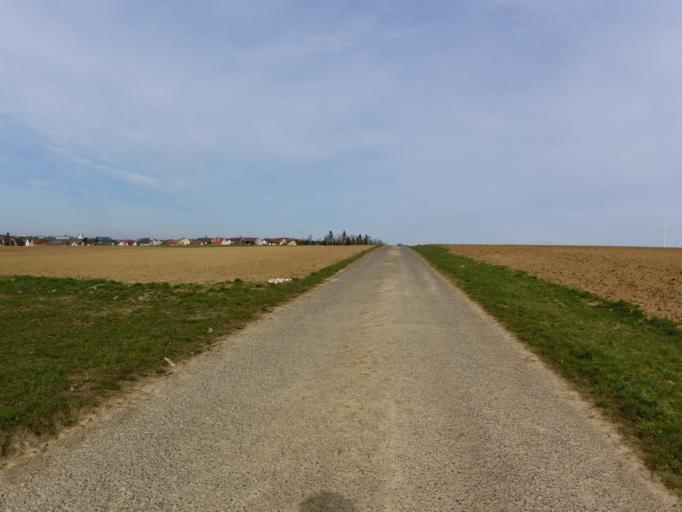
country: DE
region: Bavaria
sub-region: Regierungsbezirk Unterfranken
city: Biebelried
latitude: 49.7594
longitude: 10.0904
